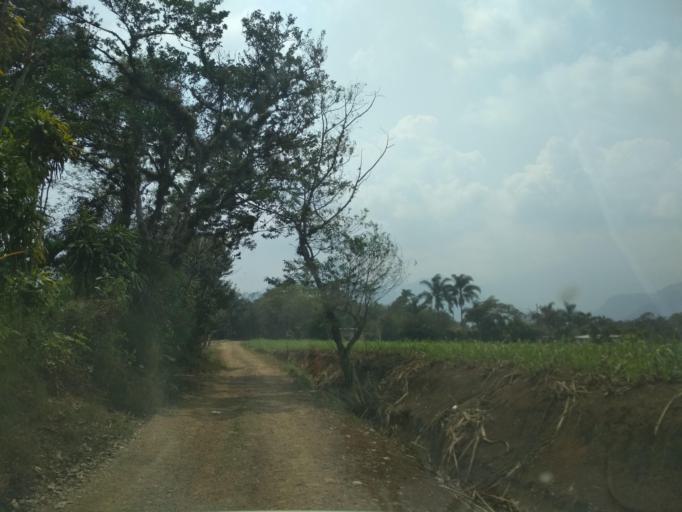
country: MX
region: Veracruz
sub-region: Cordoba
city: Fredepo
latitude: 18.8590
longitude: -96.9805
